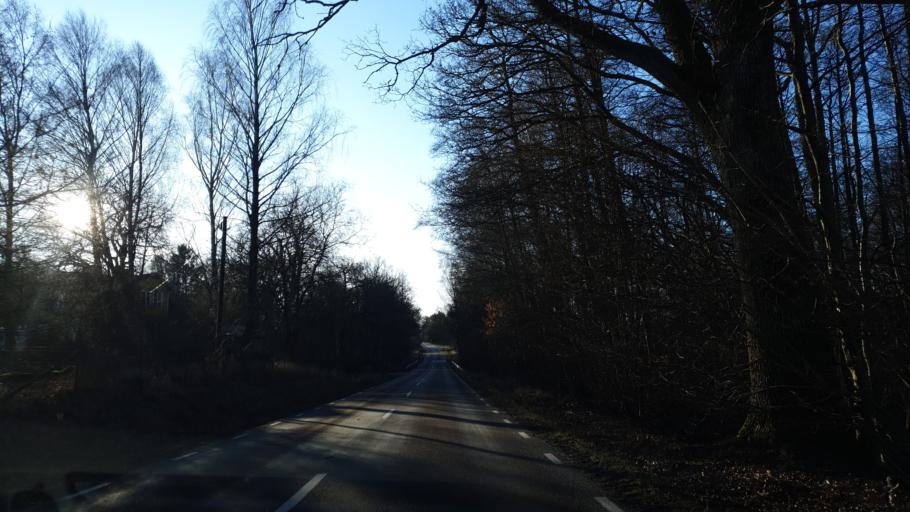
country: SE
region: Blekinge
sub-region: Karlskrona Kommun
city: Nattraby
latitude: 56.2314
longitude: 15.4127
